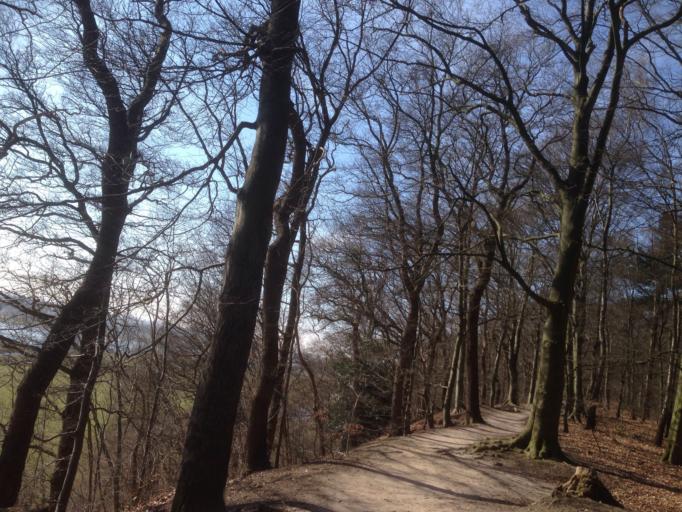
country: NL
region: Gelderland
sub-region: Gemeente Overbetuwe
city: Randwijk
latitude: 51.9658
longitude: 5.7019
